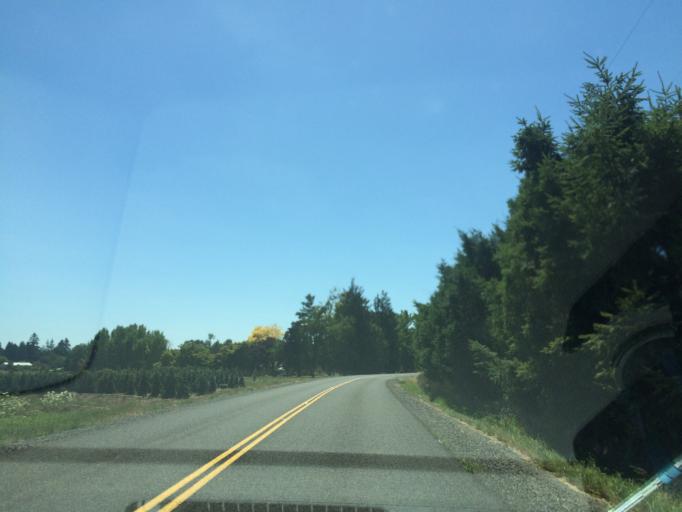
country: US
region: Oregon
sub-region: Marion County
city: Hubbard
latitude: 45.2521
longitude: -122.8477
